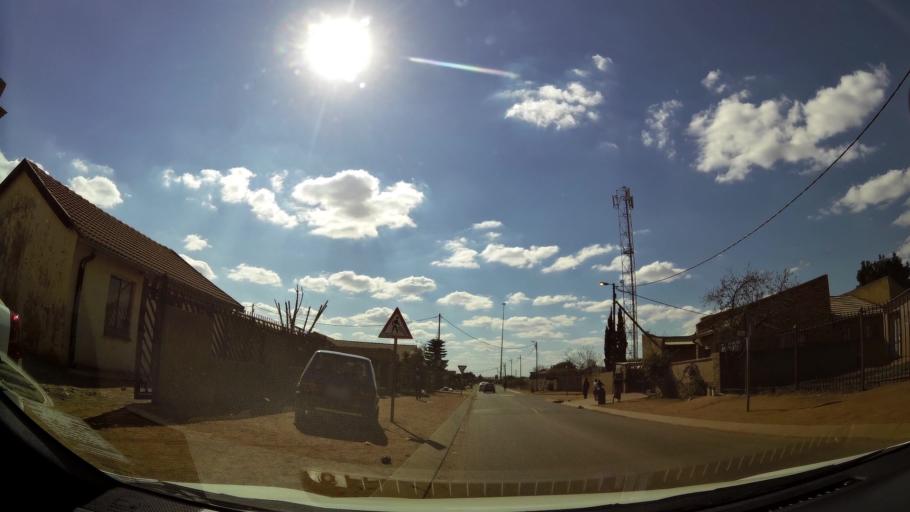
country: ZA
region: Gauteng
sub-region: City of Tshwane Metropolitan Municipality
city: Cullinan
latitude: -25.7223
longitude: 28.4035
